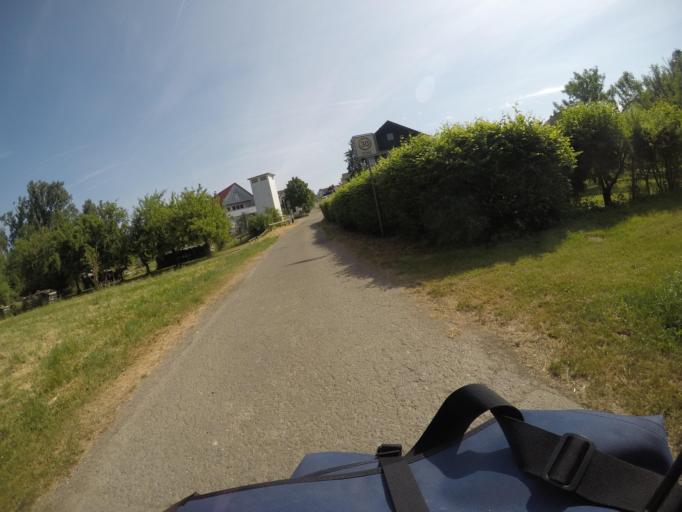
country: DE
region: Baden-Wuerttemberg
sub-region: Karlsruhe Region
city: Bietigheim
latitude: 48.9130
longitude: 8.2400
